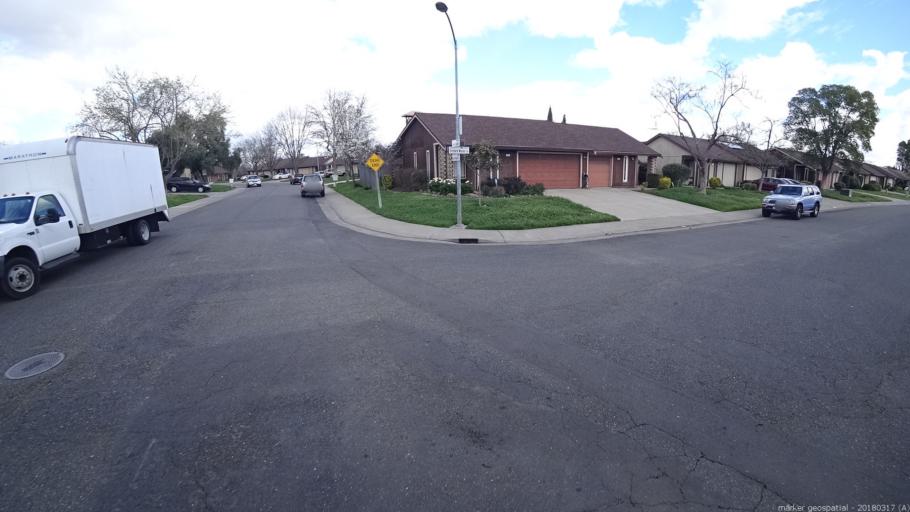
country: US
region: California
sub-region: Sacramento County
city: Florin
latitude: 38.4795
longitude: -121.4129
